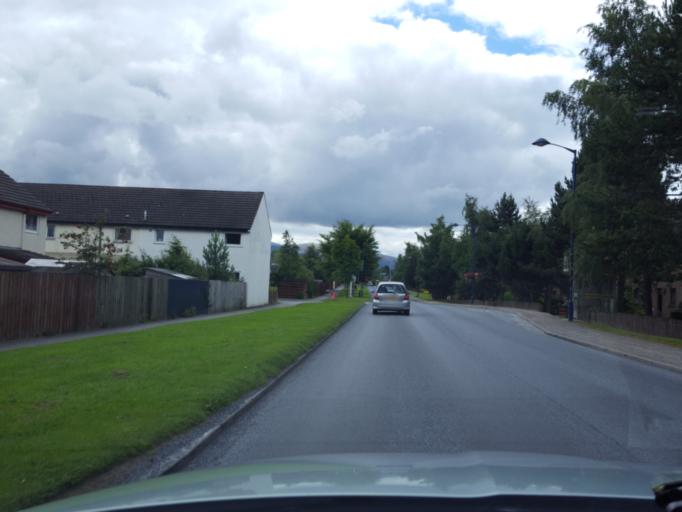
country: GB
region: Scotland
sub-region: Highland
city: Aviemore
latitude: 57.2005
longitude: -3.8282
